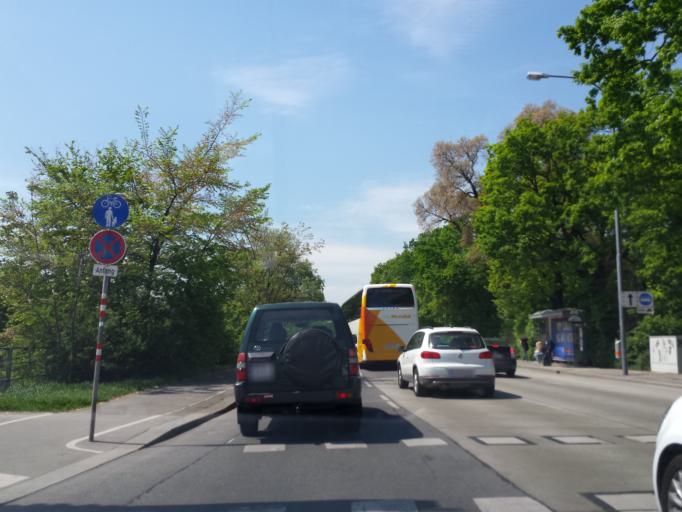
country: AT
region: Vienna
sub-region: Wien Stadt
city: Vienna
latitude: 48.1861
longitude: 16.3201
